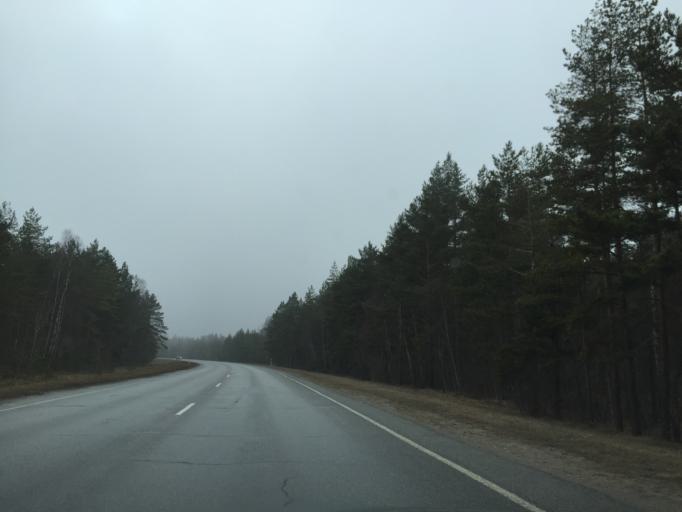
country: EE
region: Laeaene
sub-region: Lihula vald
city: Lihula
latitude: 58.6060
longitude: 23.5592
